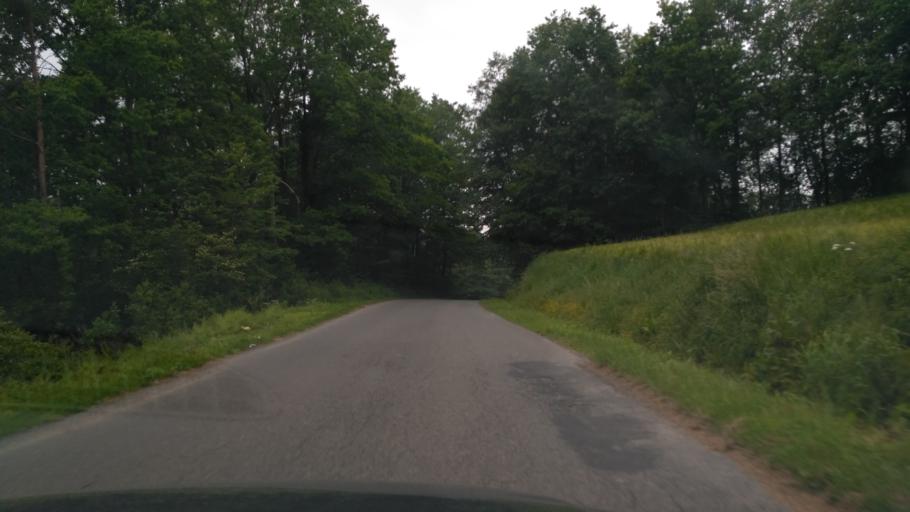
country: PL
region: Subcarpathian Voivodeship
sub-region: Powiat ropczycko-sedziszowski
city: Zagorzyce
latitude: 50.0110
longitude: 21.6768
